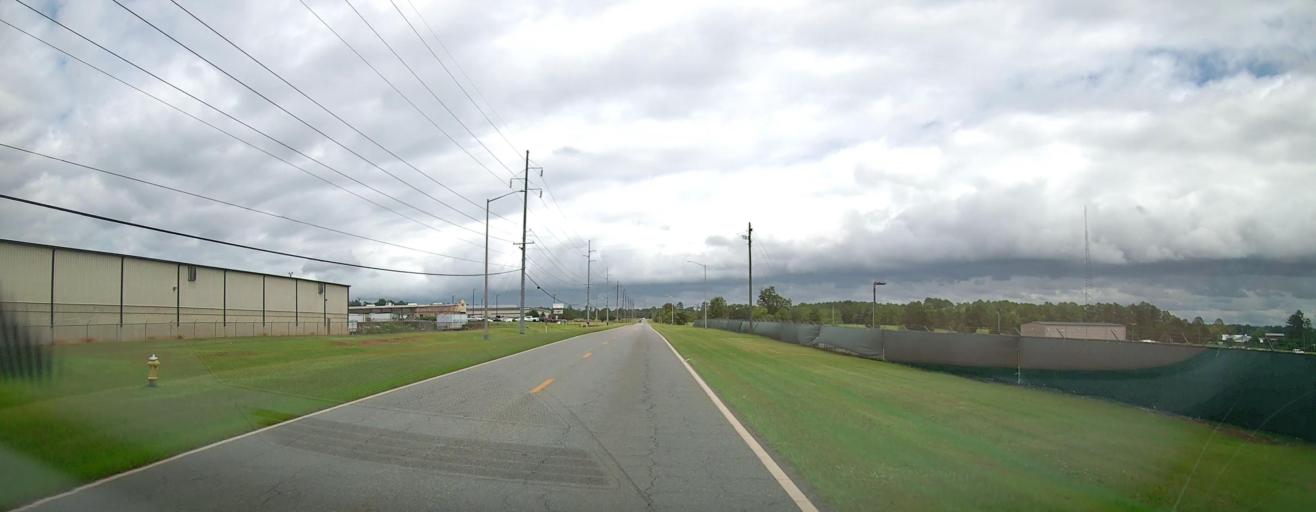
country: US
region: Georgia
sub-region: Bibb County
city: Macon
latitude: 32.8059
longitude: -83.5504
